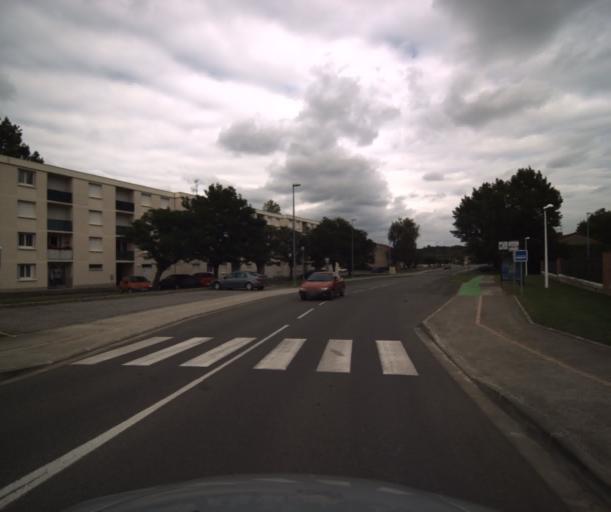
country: FR
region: Midi-Pyrenees
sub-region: Departement de la Haute-Garonne
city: Muret
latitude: 43.4499
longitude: 1.3166
